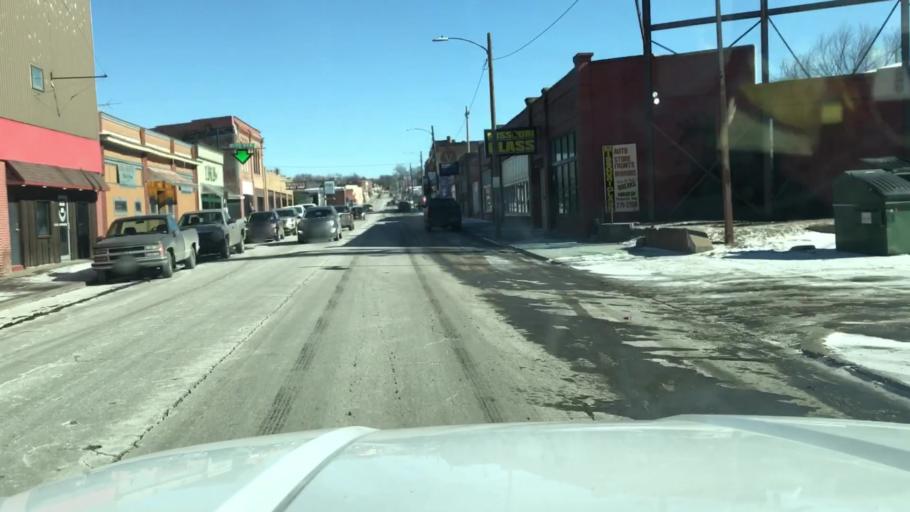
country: US
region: Missouri
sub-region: Buchanan County
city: Saint Joseph
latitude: 39.7733
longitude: -94.8387
